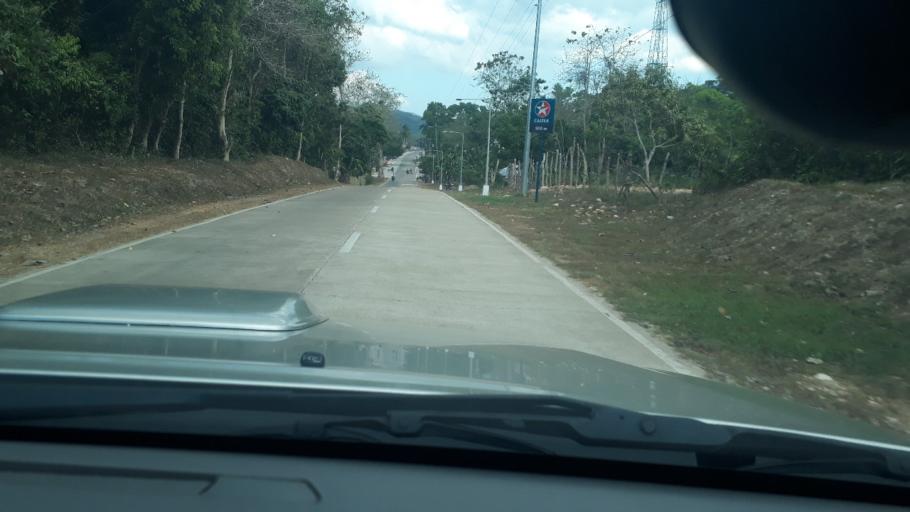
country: PH
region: Mimaropa
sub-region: Province of Palawan
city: Salvacion
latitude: 12.1272
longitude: 119.9380
